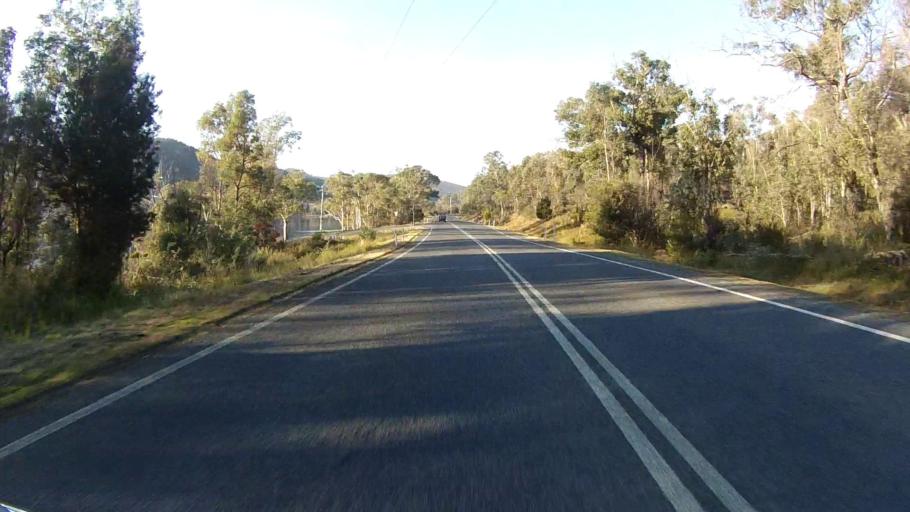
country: AU
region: Tasmania
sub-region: Clarence
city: Sandford
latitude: -43.0251
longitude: 147.8819
